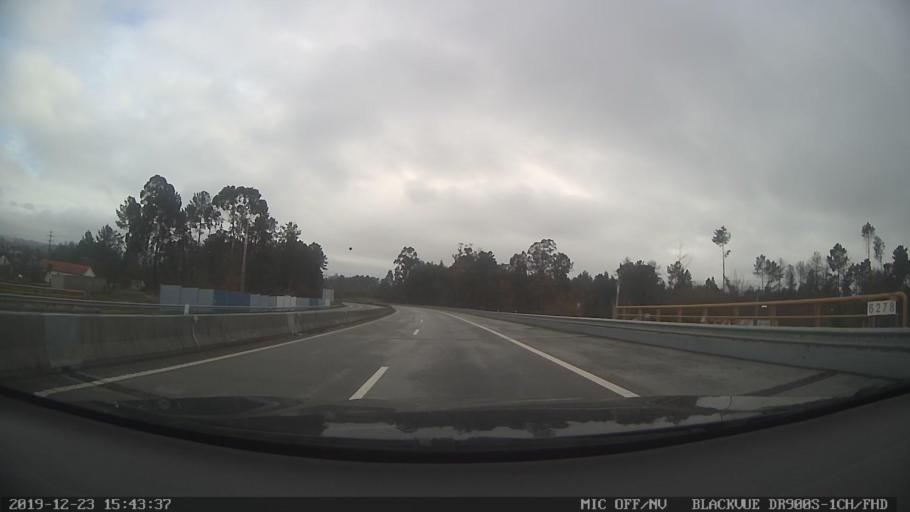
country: PT
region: Viseu
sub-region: Viseu
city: Abraveses
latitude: 40.6643
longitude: -7.9699
